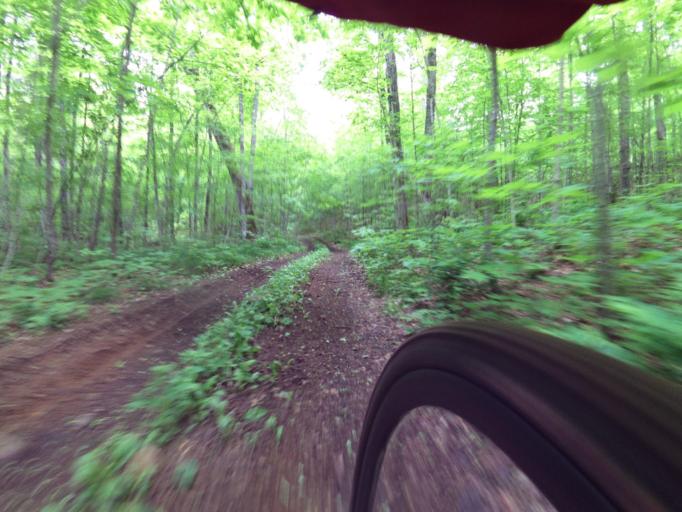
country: CA
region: Ontario
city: Arnprior
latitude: 45.1827
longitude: -76.5323
